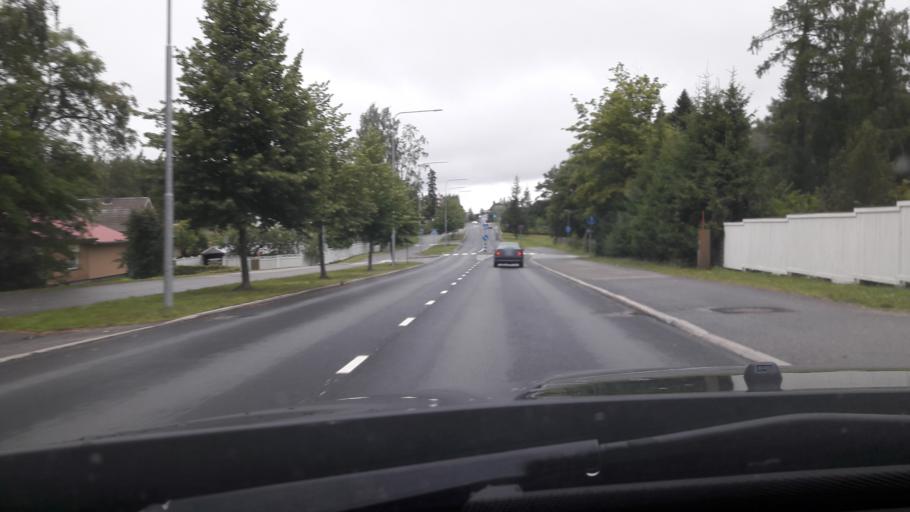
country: FI
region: North Karelia
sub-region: Joensuu
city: Joensuu
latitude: 62.5860
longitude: 29.7936
